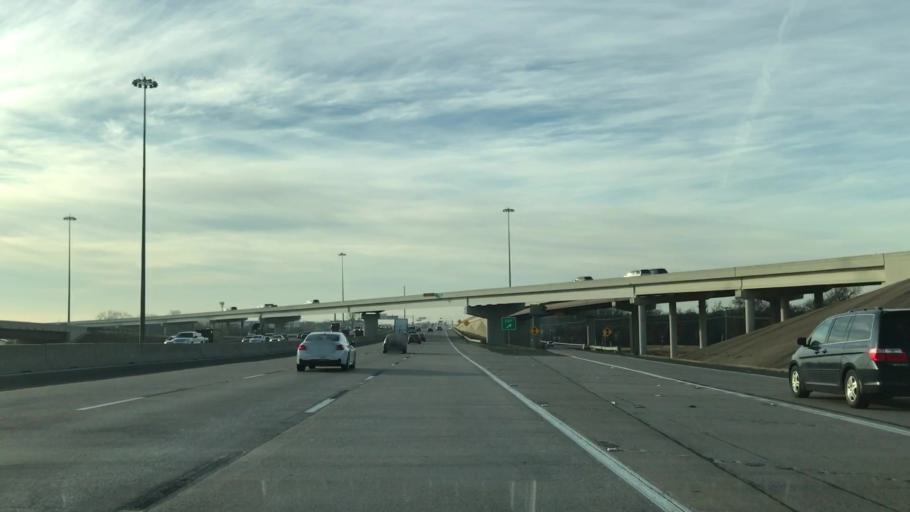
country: US
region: Texas
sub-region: Tarrant County
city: Grapevine
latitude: 32.9067
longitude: -97.0993
